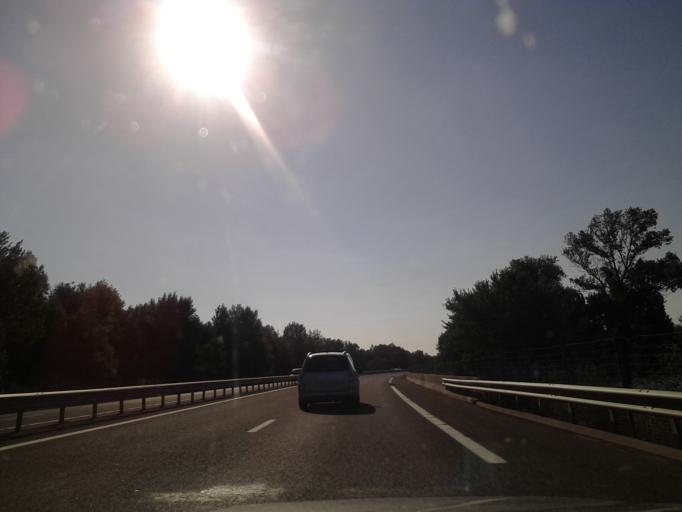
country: FR
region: Languedoc-Roussillon
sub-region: Departement des Pyrenees-Orientales
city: Millas
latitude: 42.6981
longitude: 2.6870
